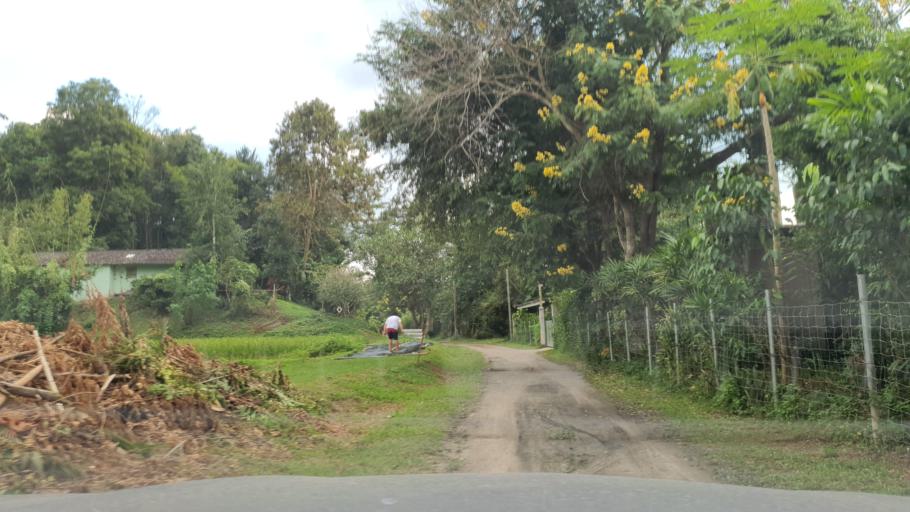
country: TH
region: Chiang Mai
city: Mae On
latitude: 18.8833
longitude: 99.2670
